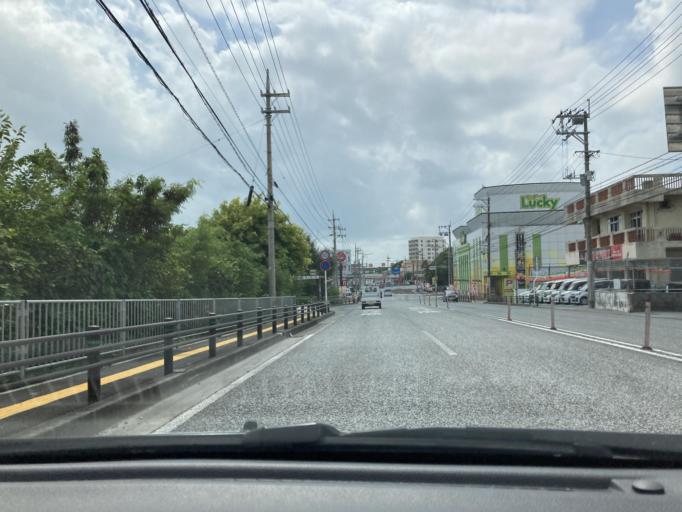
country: JP
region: Okinawa
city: Okinawa
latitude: 26.3208
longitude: 127.8217
